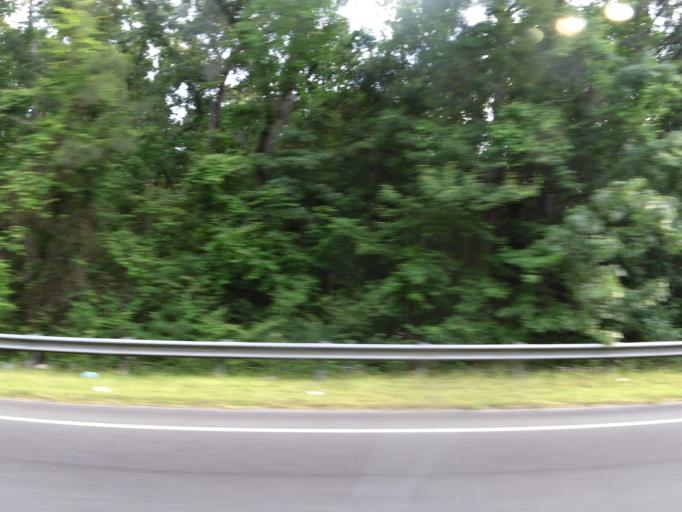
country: US
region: Georgia
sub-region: Chatham County
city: Pooler
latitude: 32.0956
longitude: -81.2104
